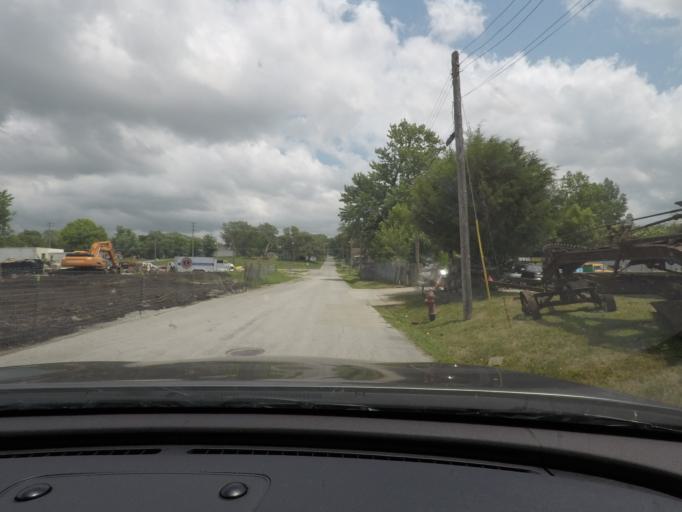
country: US
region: Missouri
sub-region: Carroll County
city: Carrollton
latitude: 39.3578
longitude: -93.4902
